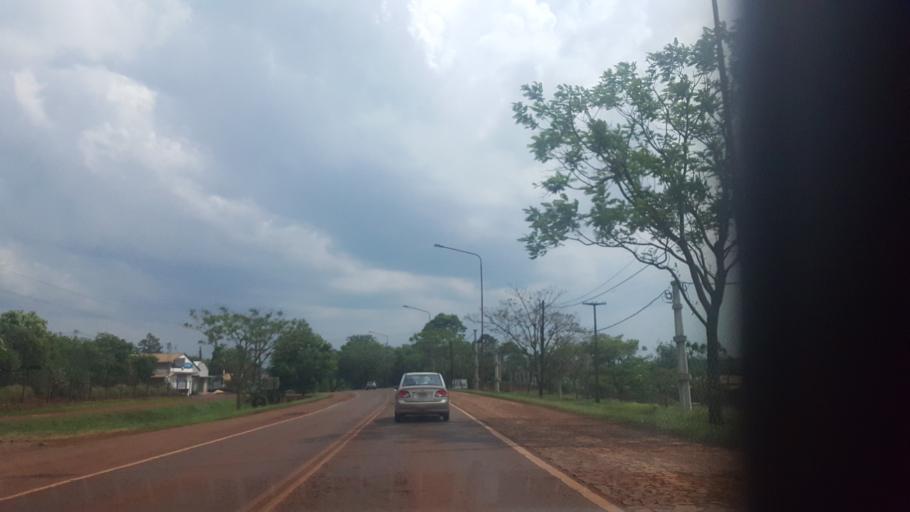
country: AR
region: Misiones
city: Jardin America
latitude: -27.0485
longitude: -55.2453
